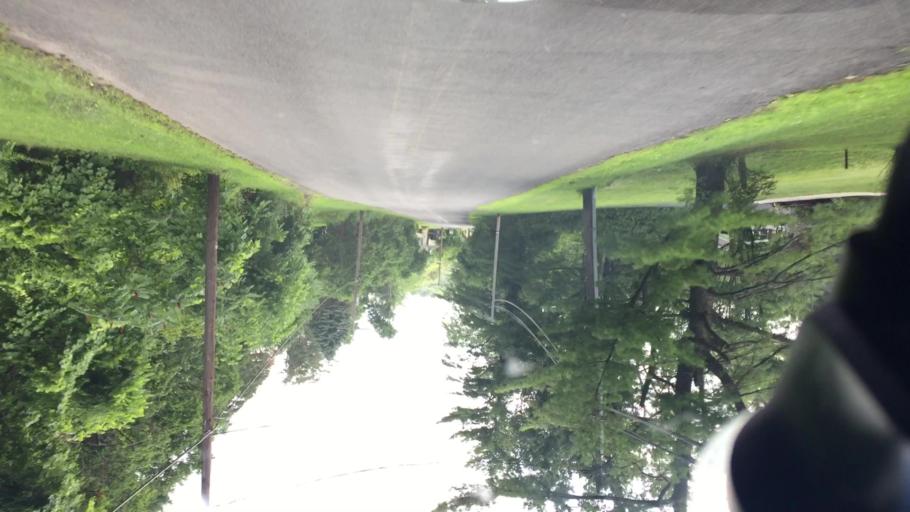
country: US
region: Pennsylvania
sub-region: Luzerne County
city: Harleigh
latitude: 41.0183
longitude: -75.9591
